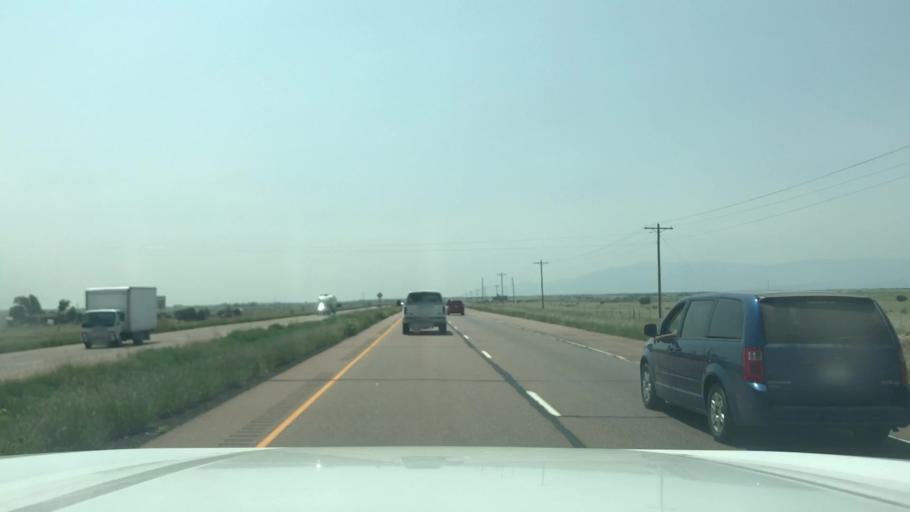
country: US
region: Colorado
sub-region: Pueblo County
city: Pueblo
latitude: 38.1003
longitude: -104.6862
